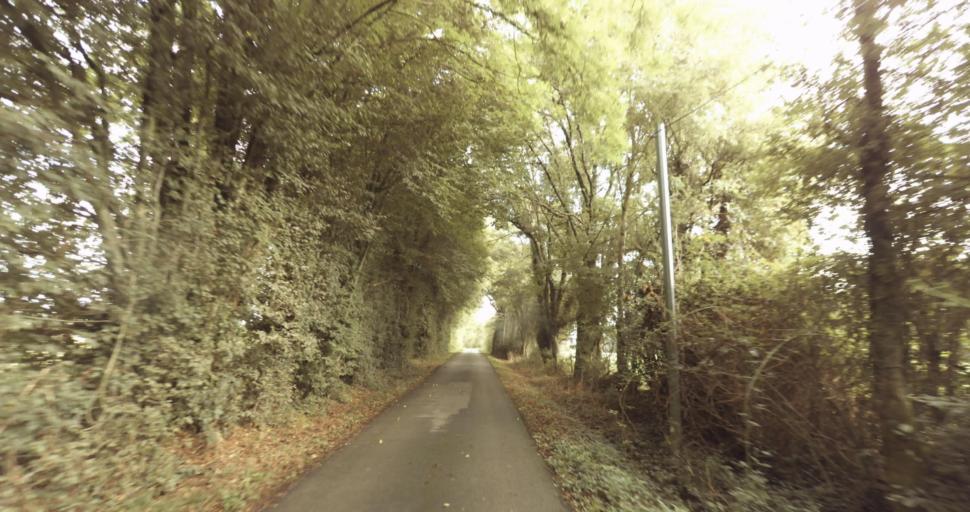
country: FR
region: Lower Normandy
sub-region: Departement de l'Orne
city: Gace
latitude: 48.8078
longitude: 0.2494
